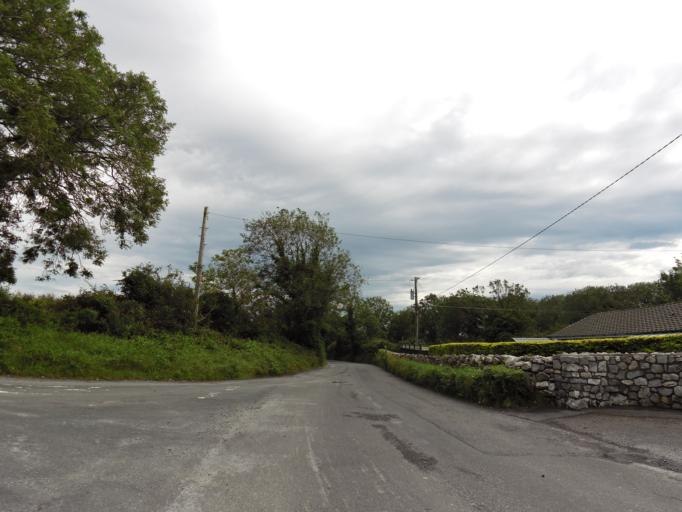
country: IE
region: Connaught
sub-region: County Galway
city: Gaillimh
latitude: 53.3136
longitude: -9.0269
